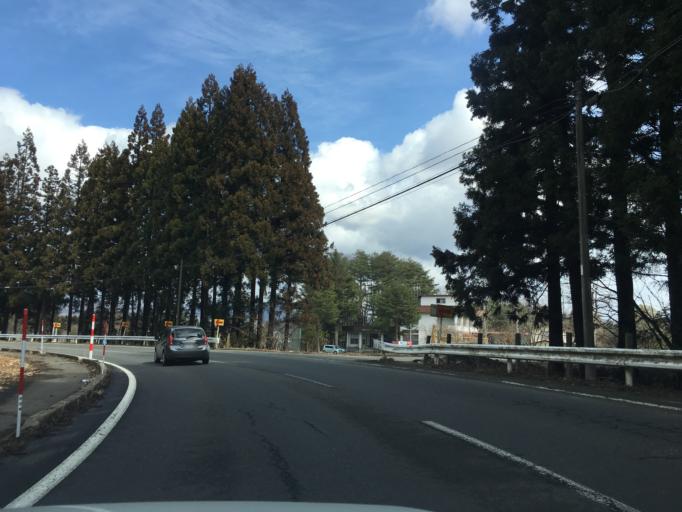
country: JP
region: Akita
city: Odate
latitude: 40.2021
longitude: 140.5549
